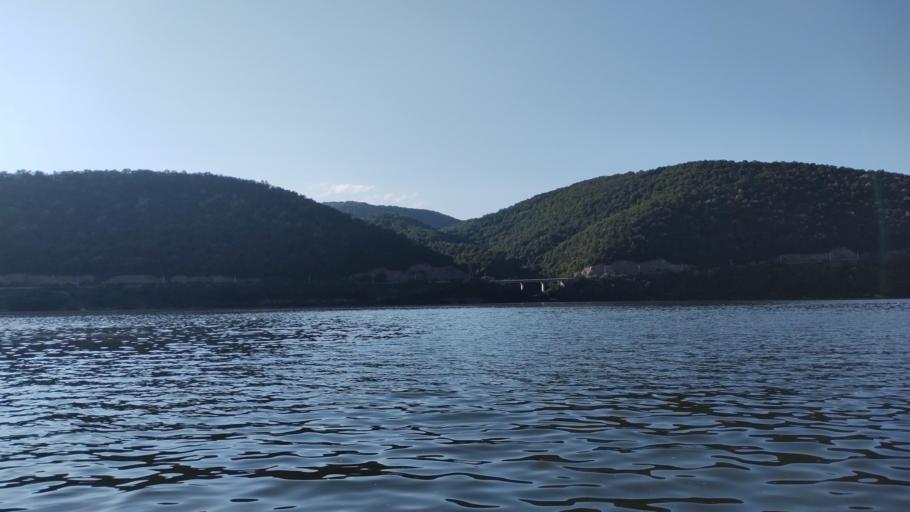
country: RO
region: Mehedinti
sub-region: Comuna Dubova
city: Dubova
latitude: 44.5812
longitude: 22.2495
